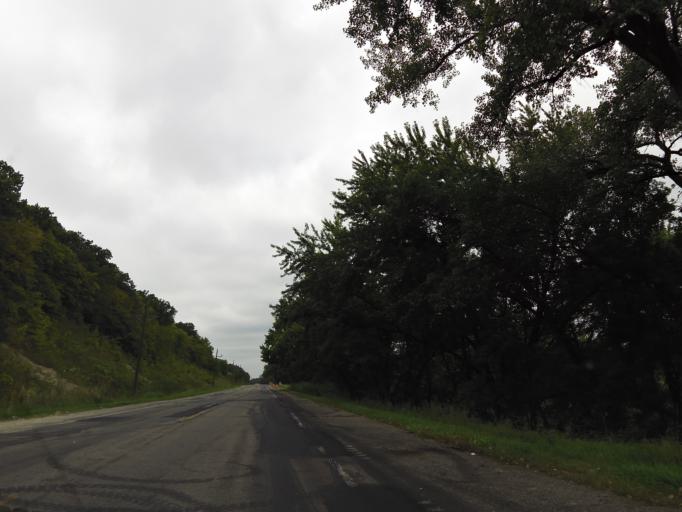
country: US
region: Minnesota
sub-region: Yellow Medicine County
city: Granite Falls
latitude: 44.8668
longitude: -95.6361
